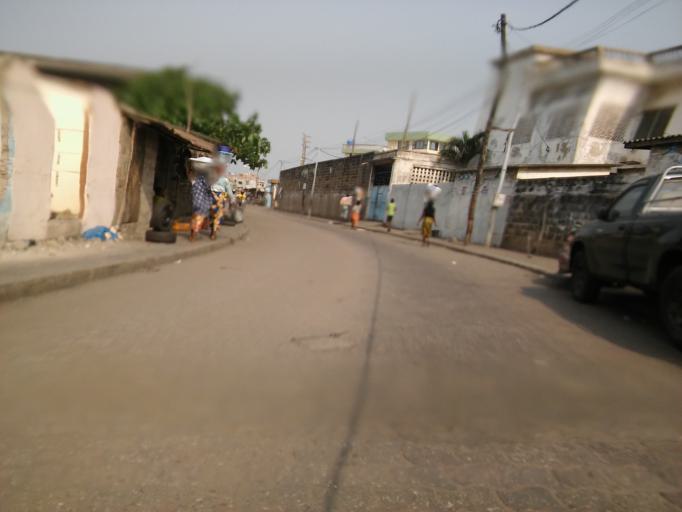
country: BJ
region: Littoral
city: Cotonou
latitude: 6.3583
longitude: 2.4459
